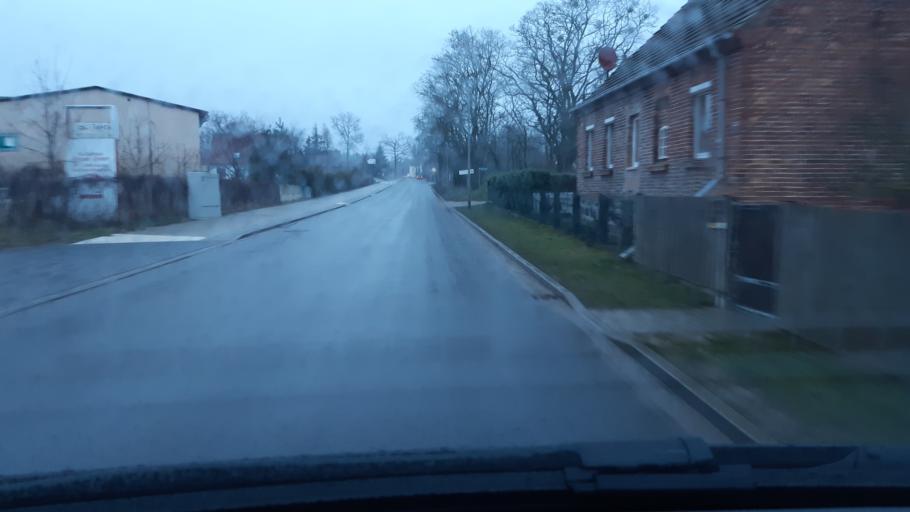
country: DE
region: Brandenburg
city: Milmersdorf
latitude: 53.1128
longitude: 13.6413
